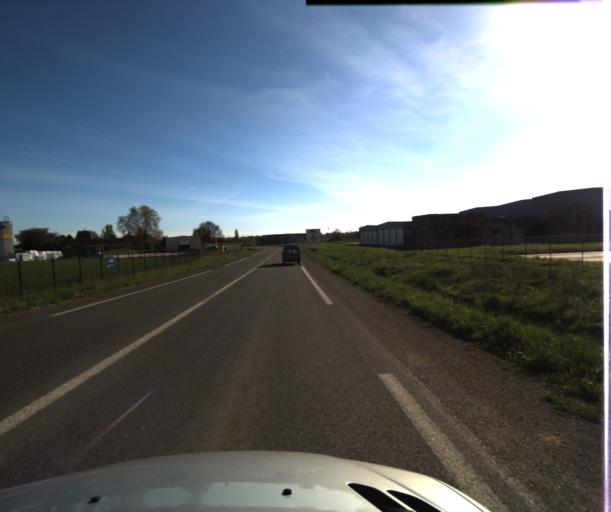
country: FR
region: Midi-Pyrenees
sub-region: Departement du Tarn-et-Garonne
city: Moissac
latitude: 44.1089
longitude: 1.1146
